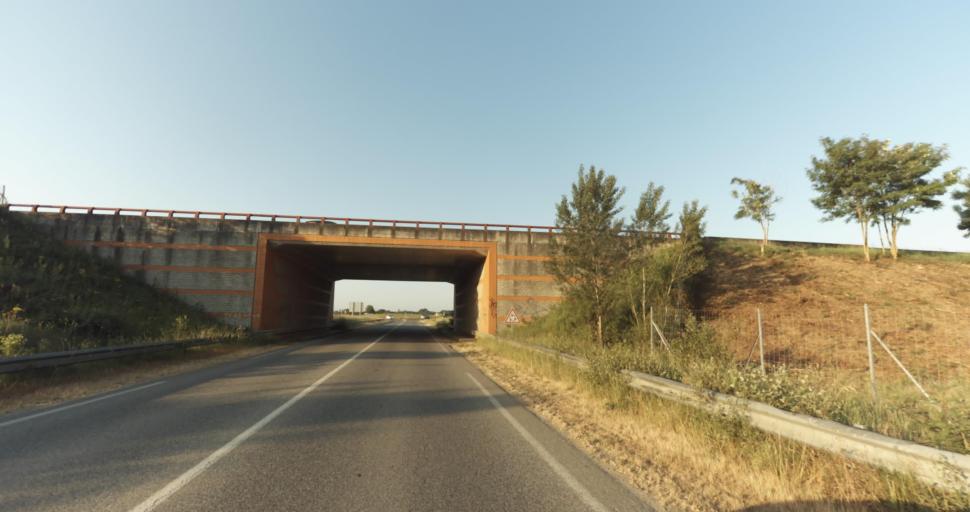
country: FR
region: Midi-Pyrenees
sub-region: Departement de la Haute-Garonne
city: Leguevin
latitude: 43.5825
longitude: 1.2182
